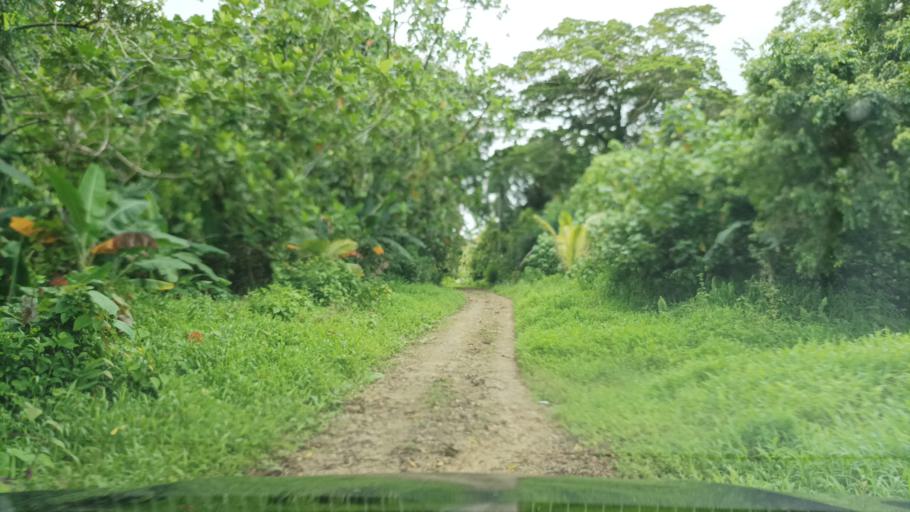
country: FM
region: Pohnpei
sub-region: Madolenihm Municipality
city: Madolenihm Municipality Government
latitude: 6.8199
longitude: 158.2832
